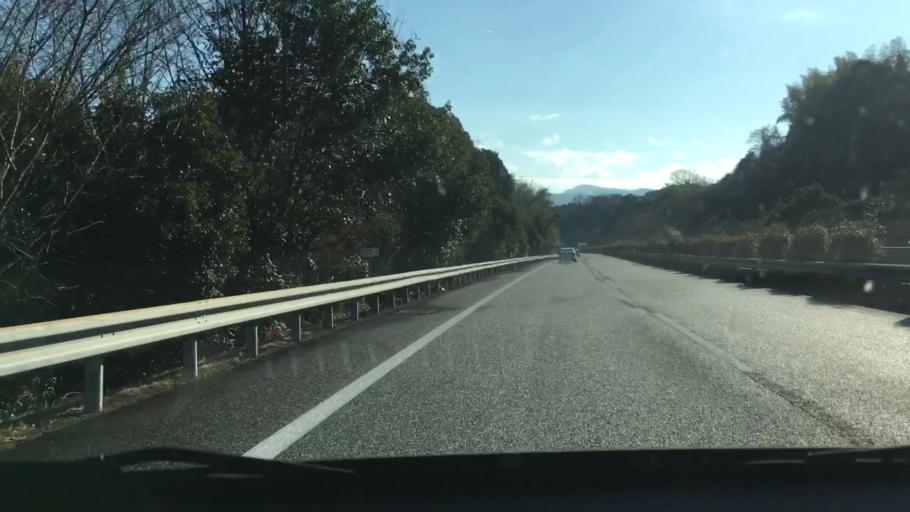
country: JP
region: Kumamoto
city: Hitoyoshi
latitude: 32.1929
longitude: 130.7776
